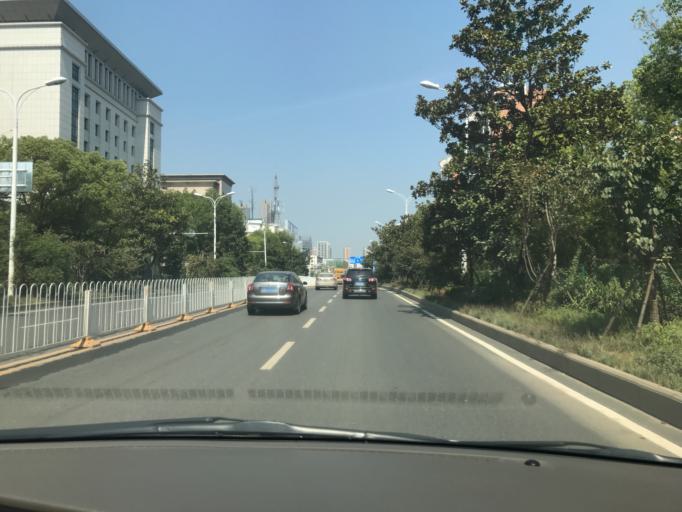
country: CN
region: Hubei
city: Shilipu
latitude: 30.5610
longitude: 114.2173
